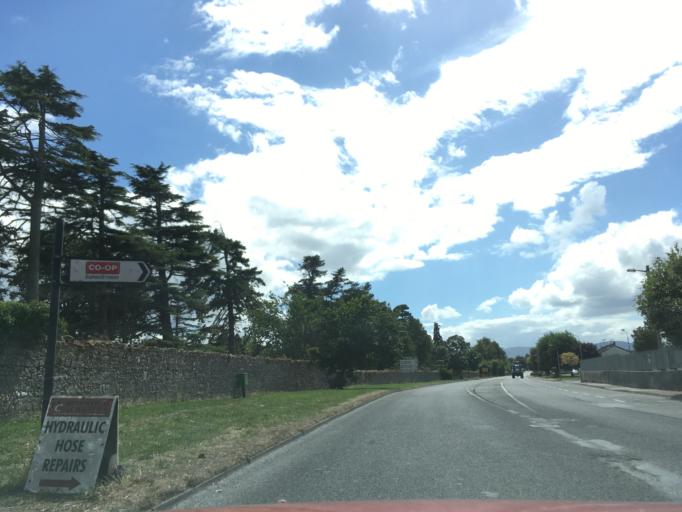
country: IE
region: Munster
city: Cahir
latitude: 52.3727
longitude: -7.9309
